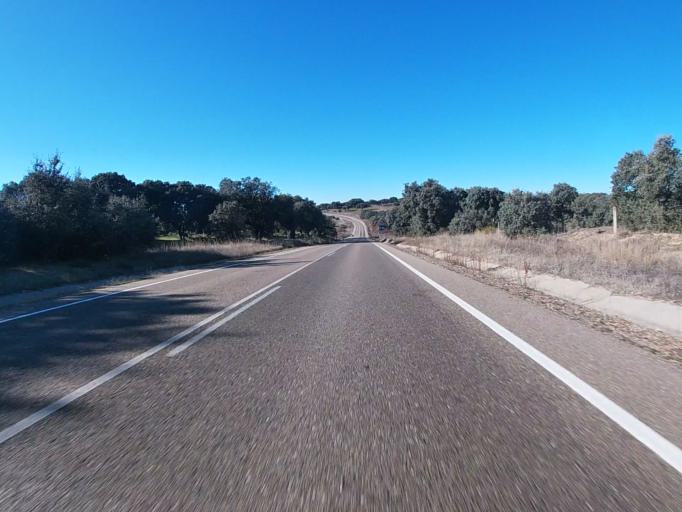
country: ES
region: Castille and Leon
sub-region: Provincia de Salamanca
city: Juzbado
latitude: 41.0771
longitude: -5.8427
